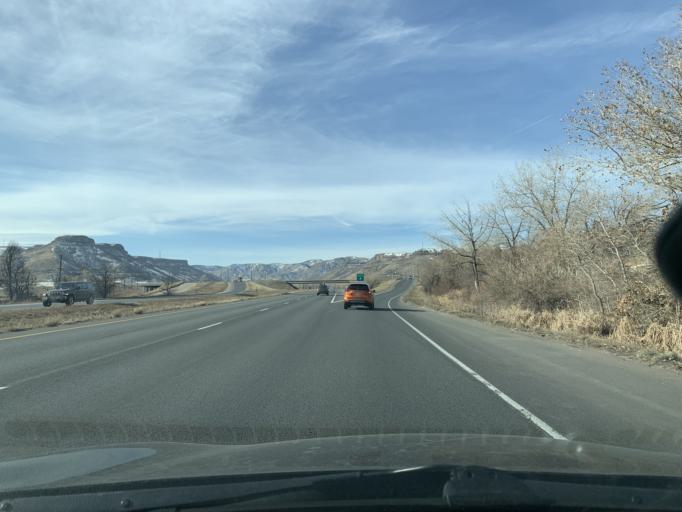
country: US
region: Colorado
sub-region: Jefferson County
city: Applewood
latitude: 39.7737
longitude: -105.1698
